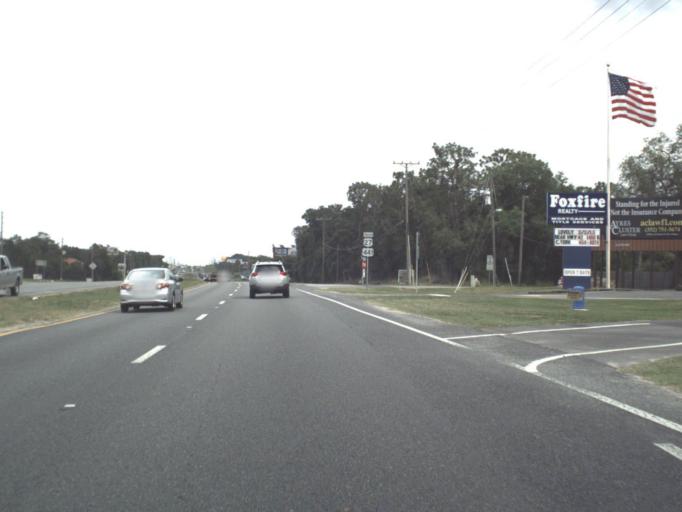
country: US
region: Florida
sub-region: Sumter County
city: The Villages
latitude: 28.9817
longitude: -81.9873
